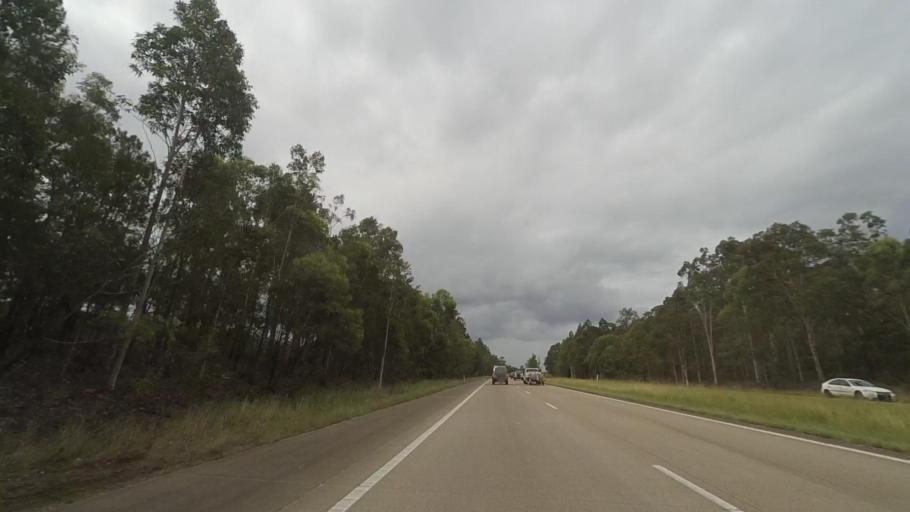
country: AU
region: New South Wales
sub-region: Port Stephens Shire
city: Raymond Terrace
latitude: -32.7219
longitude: 151.7882
